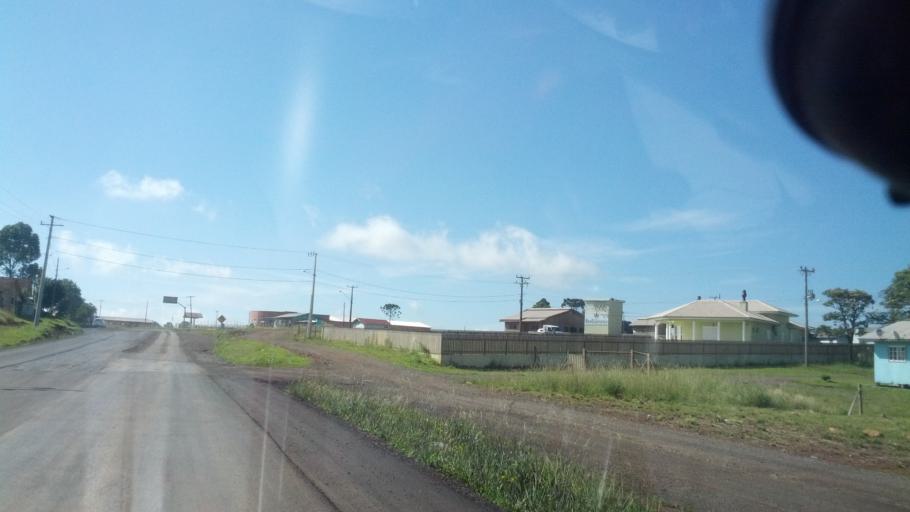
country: BR
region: Santa Catarina
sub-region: Lages
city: Lages
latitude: -27.9423
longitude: -50.5093
